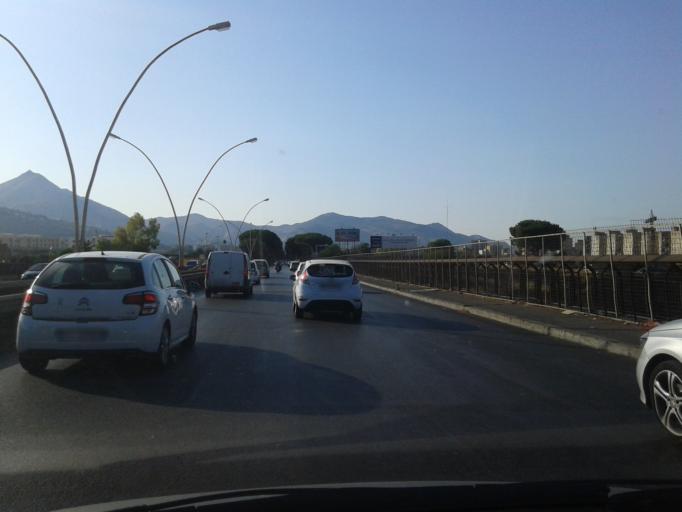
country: IT
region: Sicily
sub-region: Palermo
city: Villa Ciambra
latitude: 38.0895
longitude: 13.3452
